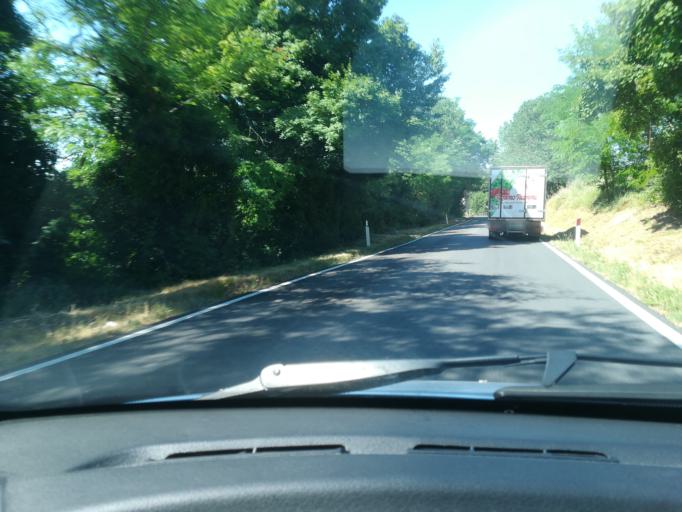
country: IT
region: The Marches
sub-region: Provincia di Macerata
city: Ripe San Ginesio
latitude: 43.1134
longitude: 13.3663
